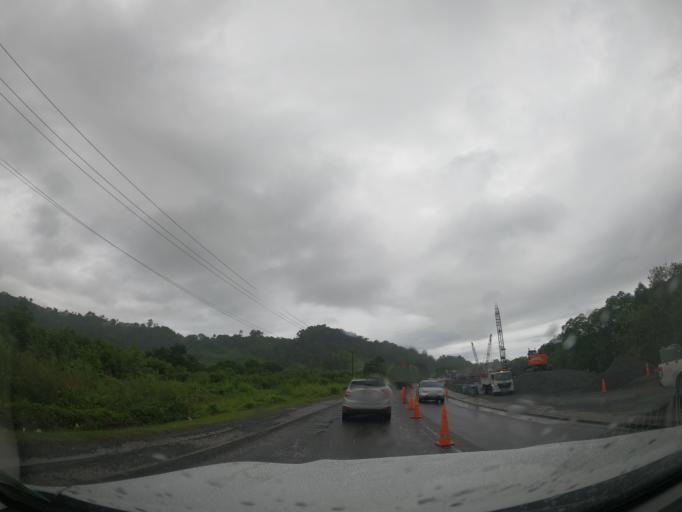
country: FJ
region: Central
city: Suva
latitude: -18.1134
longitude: 178.4305
